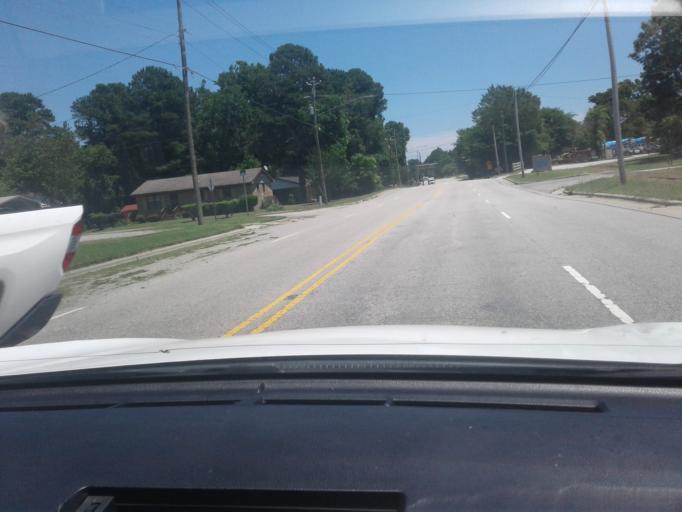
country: US
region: North Carolina
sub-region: Harnett County
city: Lillington
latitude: 35.3927
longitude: -78.8150
